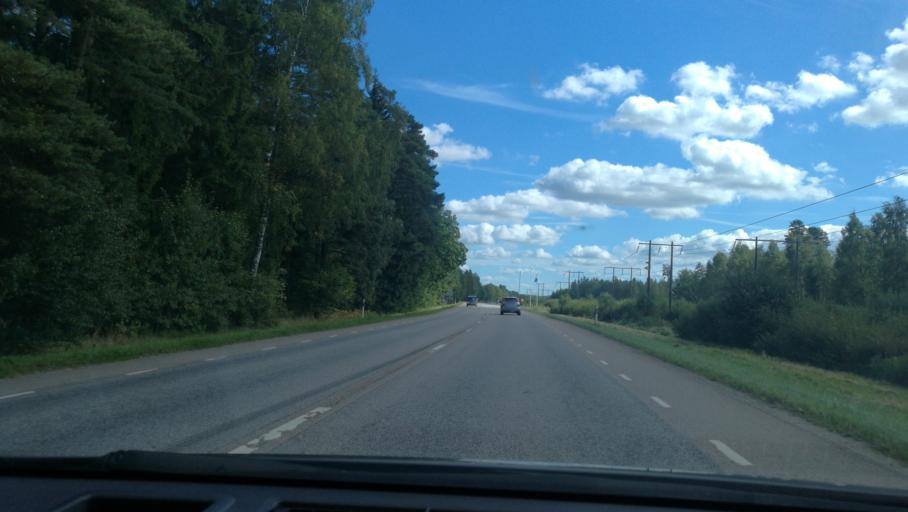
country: SE
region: Vaestra Goetaland
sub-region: Lidkopings Kommun
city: Lidkoping
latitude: 58.4936
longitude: 13.2155
